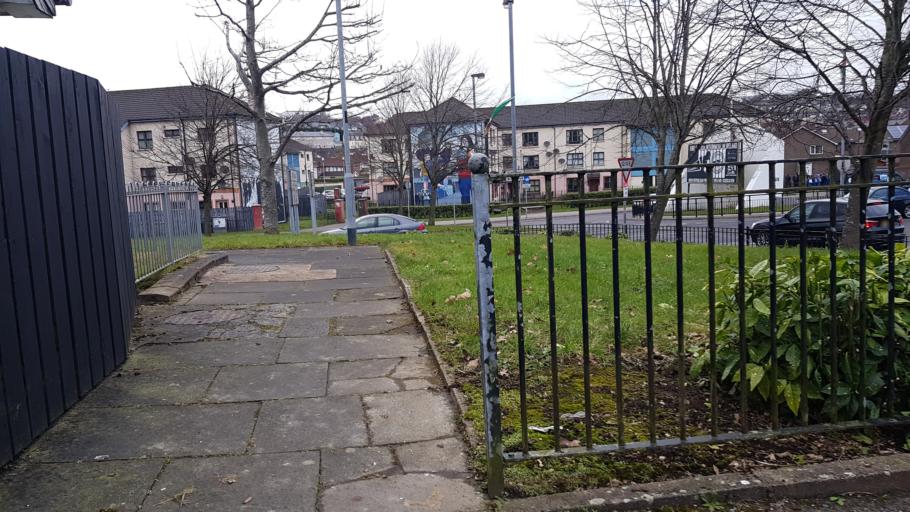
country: GB
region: Northern Ireland
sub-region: City of Derry
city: Derry
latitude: 54.9954
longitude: -7.3264
